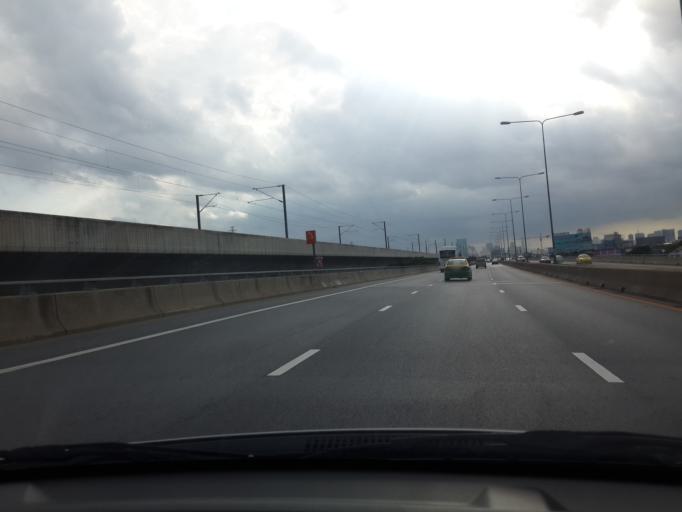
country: TH
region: Bangkok
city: Suan Luang
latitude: 13.7406
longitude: 100.6240
